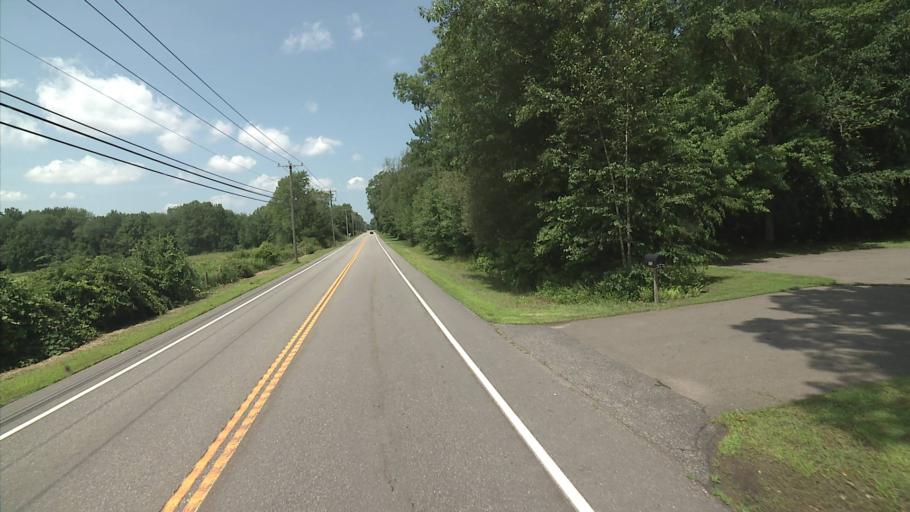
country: US
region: Connecticut
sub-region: Tolland County
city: Tolland
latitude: 41.8109
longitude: -72.3957
